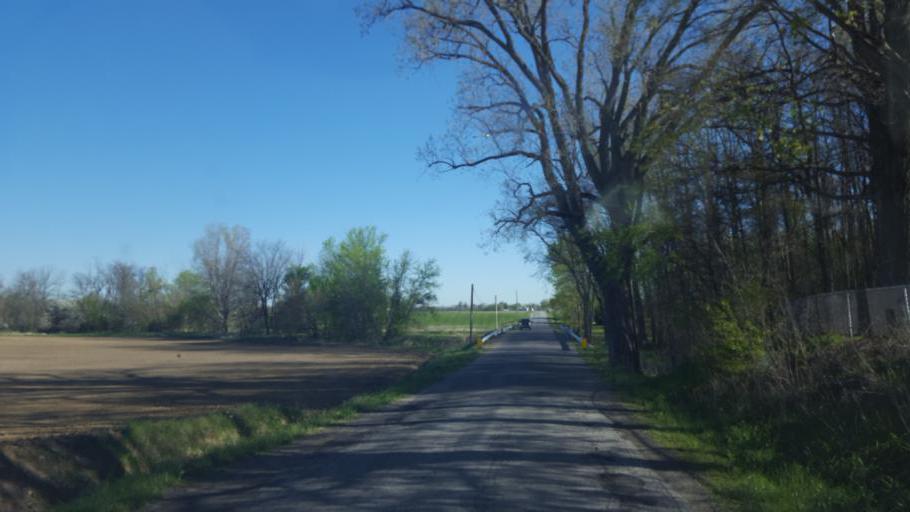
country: US
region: Ohio
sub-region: Morrow County
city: Mount Gilead
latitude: 40.6233
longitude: -82.9183
